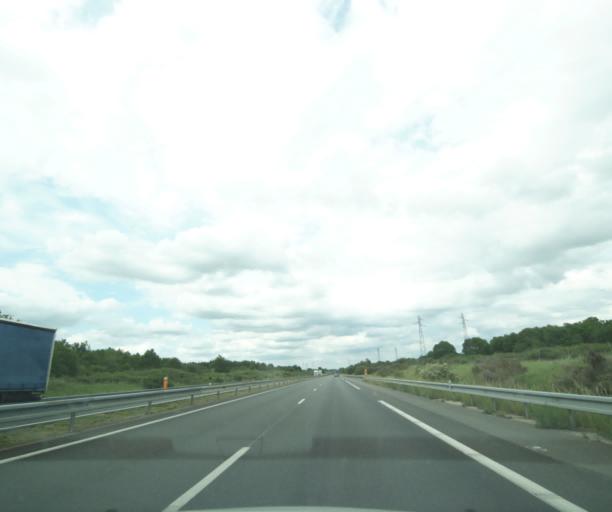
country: FR
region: Centre
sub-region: Departement du Loir-et-Cher
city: Theillay
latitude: 47.3033
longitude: 2.0465
